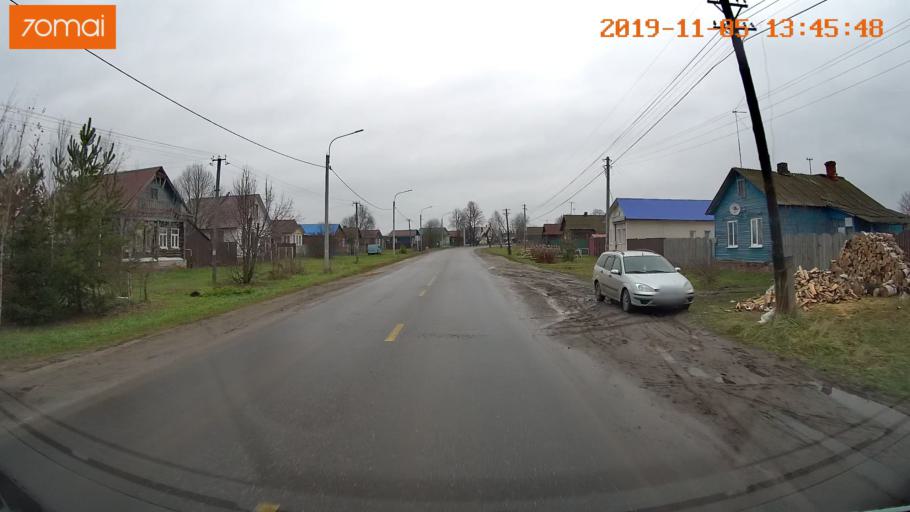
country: RU
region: Ivanovo
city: Shuya
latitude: 56.9915
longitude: 41.4114
